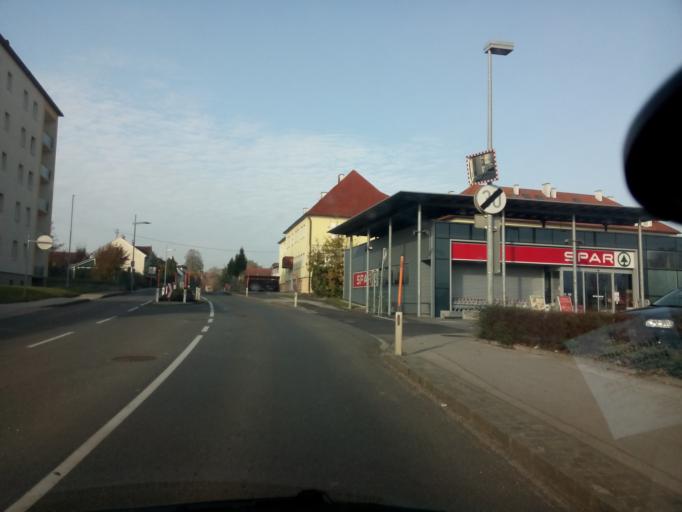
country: AT
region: Upper Austria
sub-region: Politischer Bezirk Linz-Land
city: Traun
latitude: 48.1338
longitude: 14.2268
